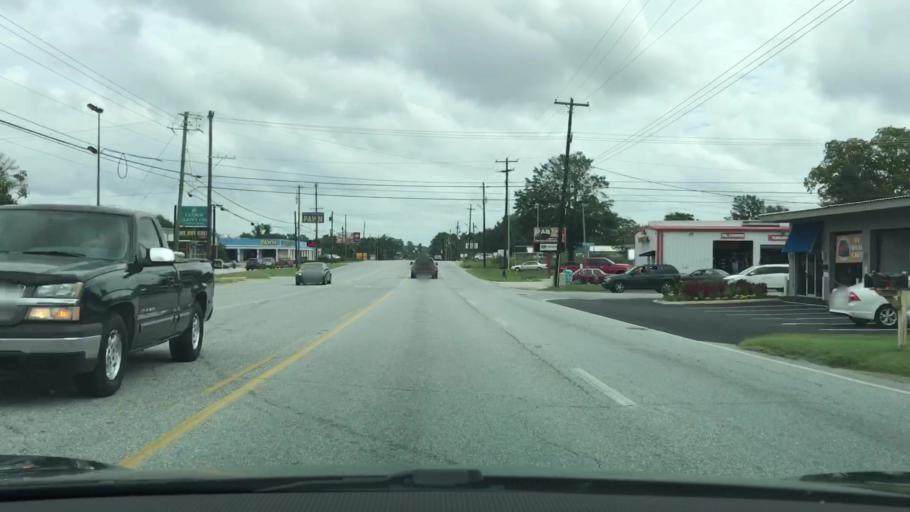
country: US
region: Alabama
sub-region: Lee County
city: Opelika
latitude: 32.6332
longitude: -85.4314
